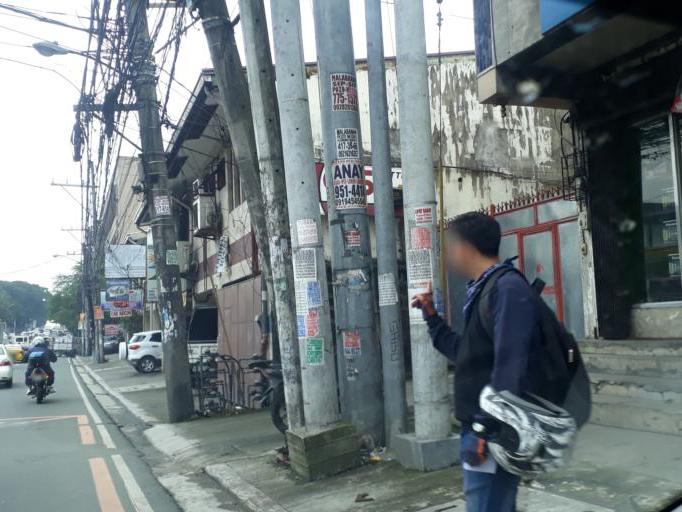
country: PH
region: Calabarzon
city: Del Monte
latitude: 14.6453
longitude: 121.0171
